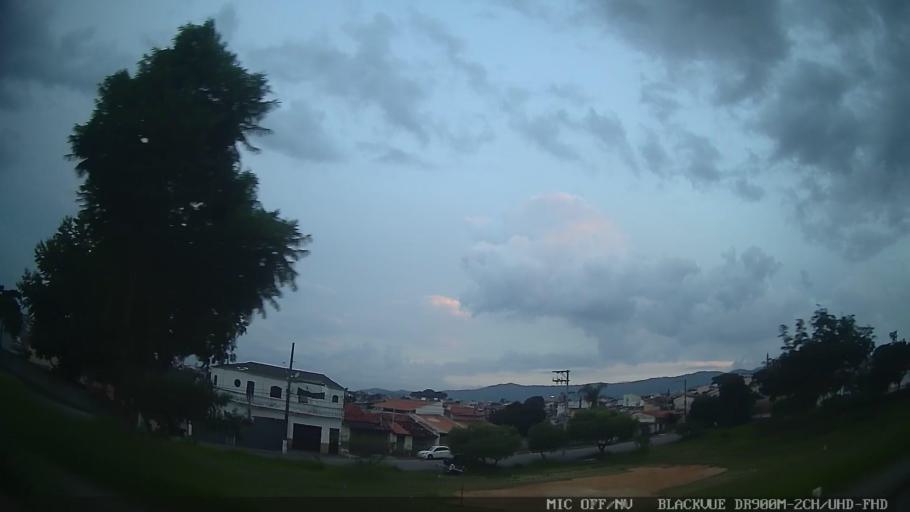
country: BR
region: Sao Paulo
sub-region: Atibaia
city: Atibaia
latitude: -23.1263
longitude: -46.5723
